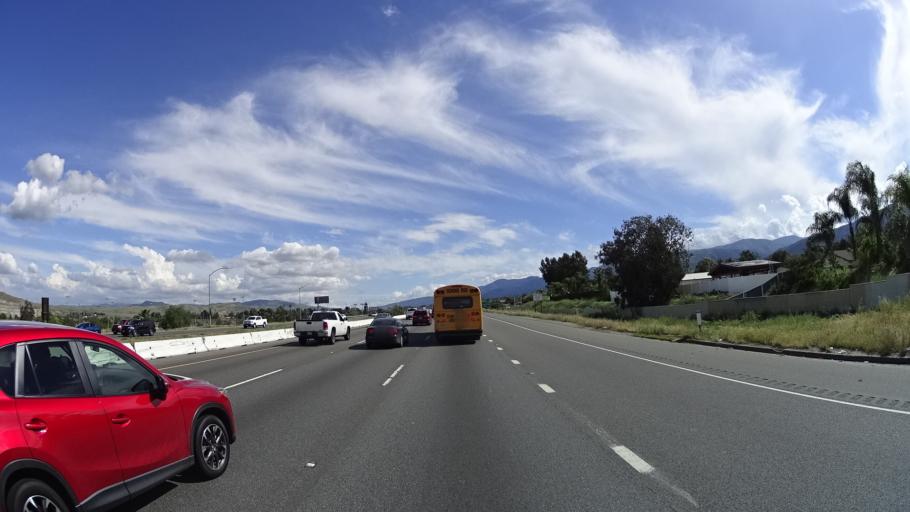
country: US
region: California
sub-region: Riverside County
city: El Cerrito
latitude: 33.8367
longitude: -117.5328
